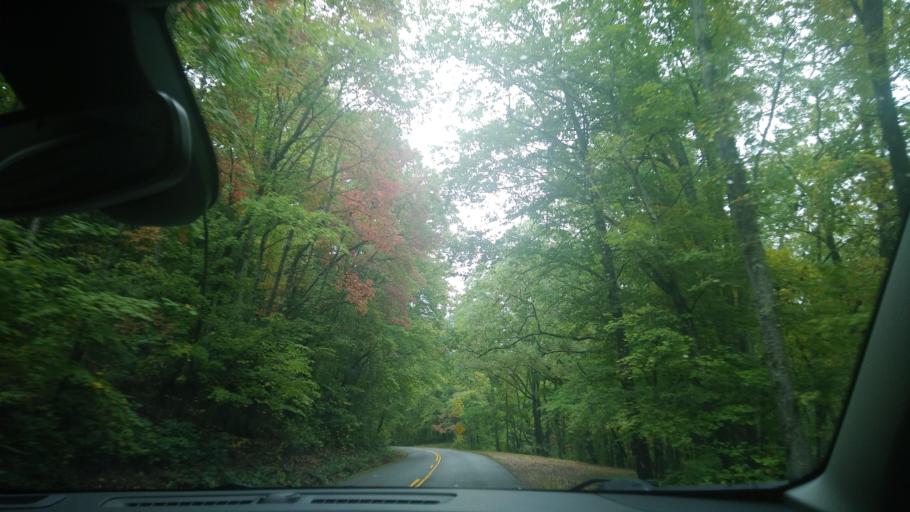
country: US
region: North Carolina
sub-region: Mitchell County
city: Spruce Pine
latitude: 35.9008
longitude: -81.9783
